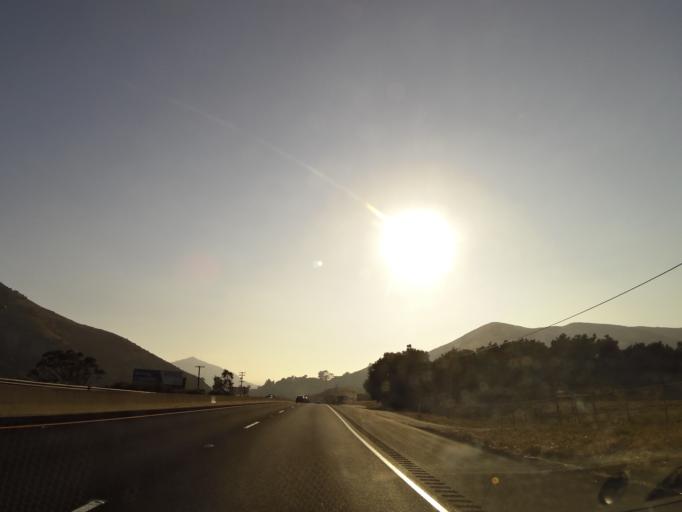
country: US
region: California
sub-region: San Luis Obispo County
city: San Luis Obispo
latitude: 35.2953
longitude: -120.6335
